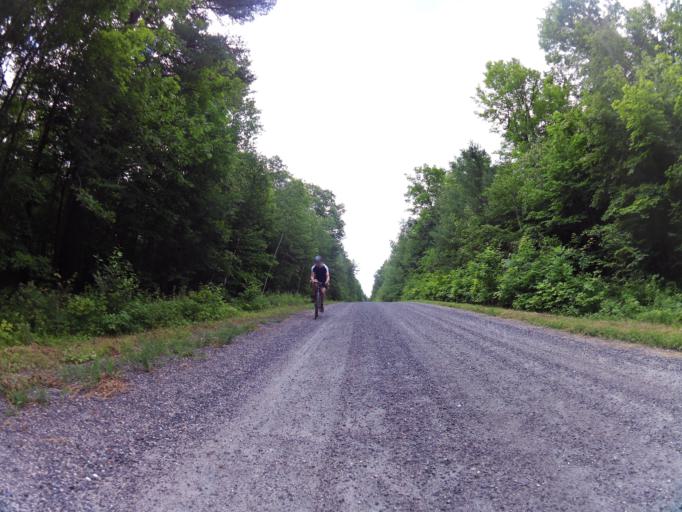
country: CA
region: Ontario
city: Perth
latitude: 45.0262
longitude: -76.5393
